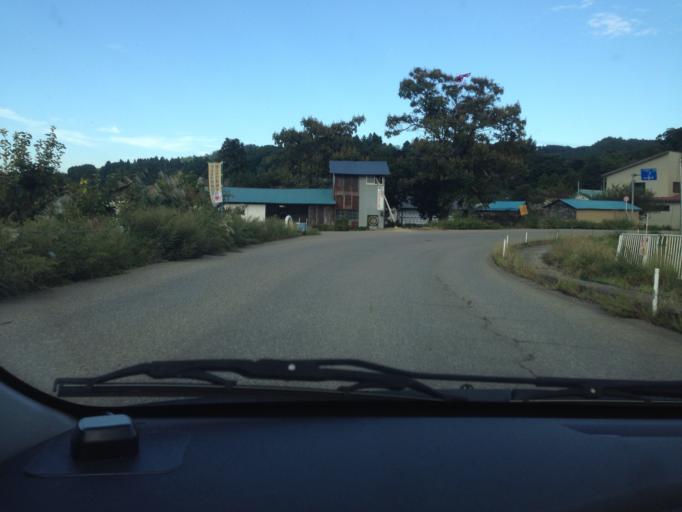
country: JP
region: Fukushima
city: Kitakata
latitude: 37.5771
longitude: 139.7670
